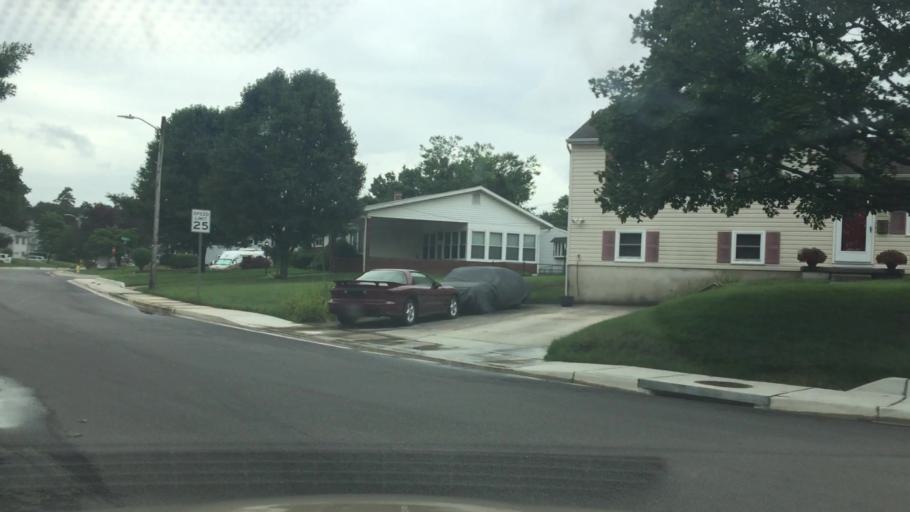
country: US
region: Maryland
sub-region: Anne Arundel County
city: South Gate
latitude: 39.1428
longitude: -76.6410
